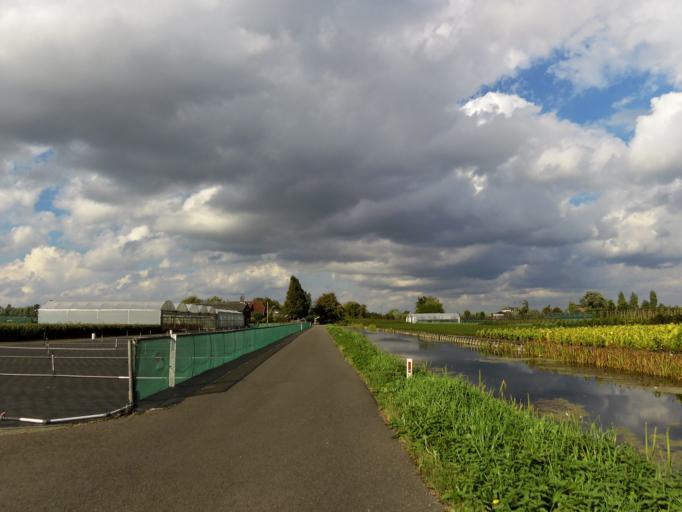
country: NL
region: South Holland
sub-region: Gemeente Boskoop
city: Boskoop
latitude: 52.0993
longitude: 4.6189
